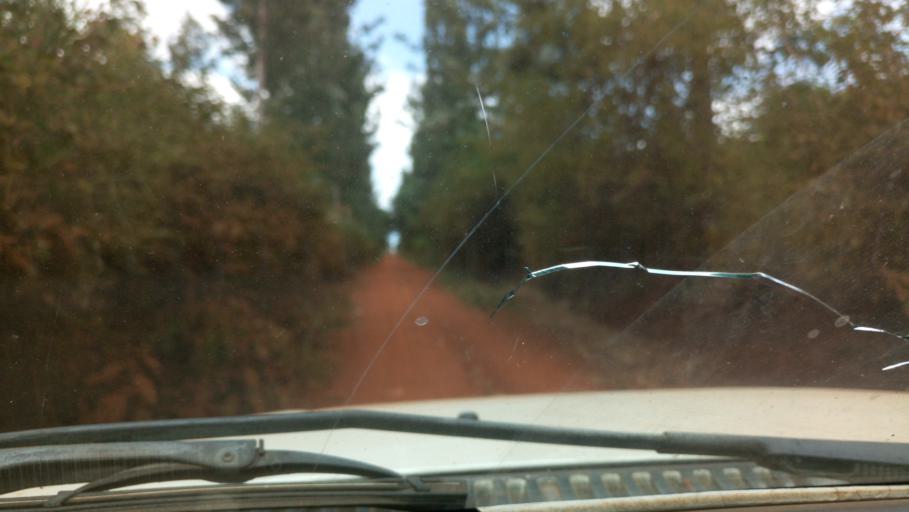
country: KE
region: Murang'a District
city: Karuri
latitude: -0.7394
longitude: 37.1947
